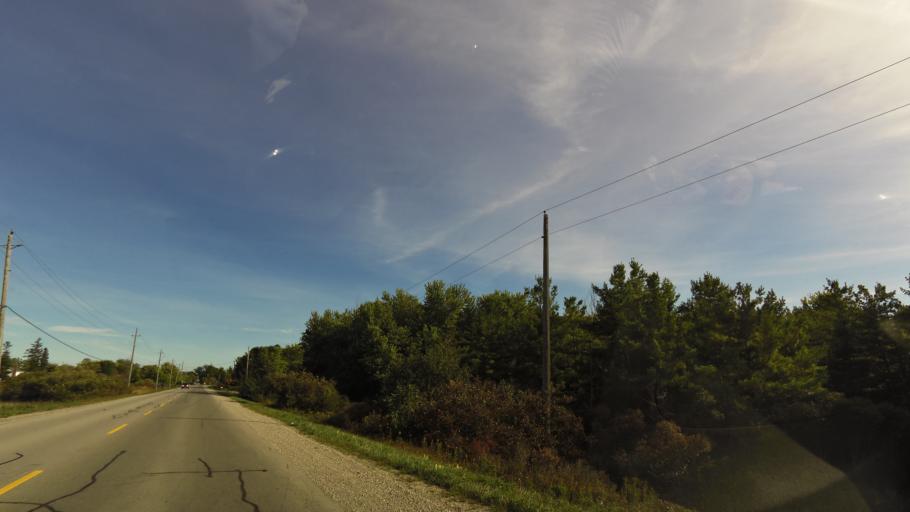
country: CA
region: Ontario
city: Ancaster
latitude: 43.0253
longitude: -80.0000
